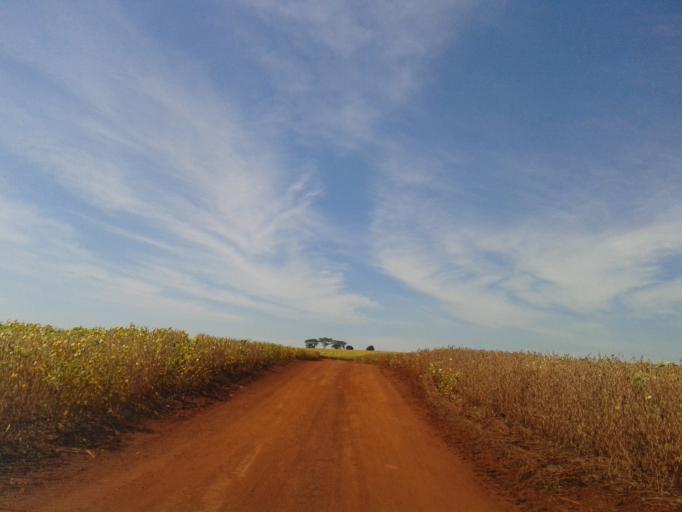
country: BR
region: Minas Gerais
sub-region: Capinopolis
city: Capinopolis
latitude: -18.6534
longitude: -49.7029
